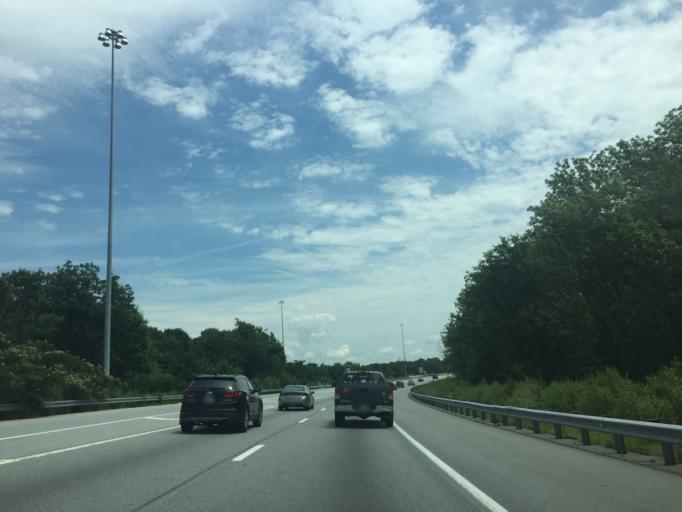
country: US
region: Delaware
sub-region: New Castle County
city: Wilmington Manor
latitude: 39.7014
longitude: -75.5906
